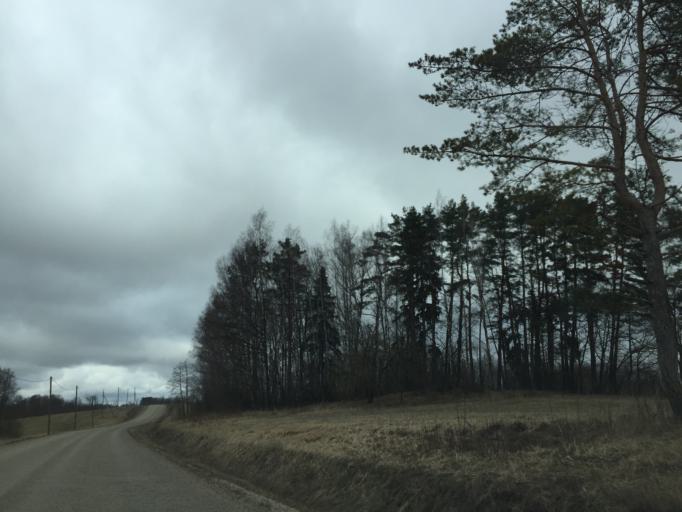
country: LV
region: Ilukste
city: Ilukste
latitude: 56.0354
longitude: 26.2054
